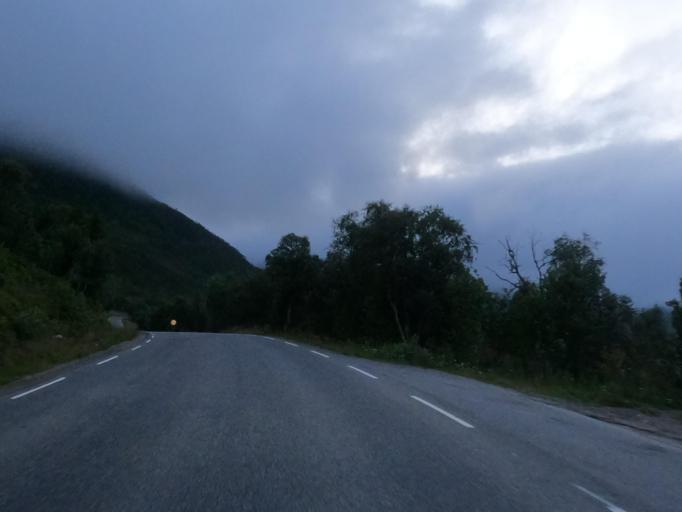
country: NO
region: Nordland
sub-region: Lodingen
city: Lodingen
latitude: 68.6023
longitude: 15.7870
